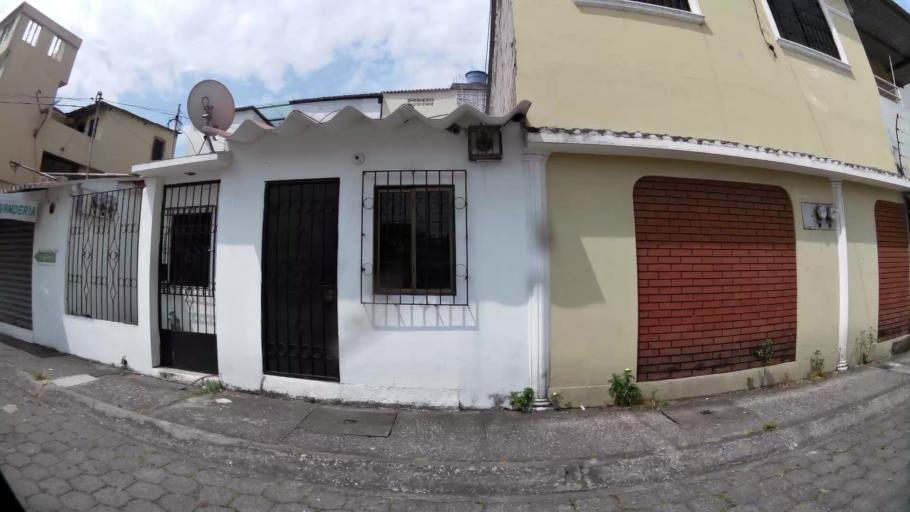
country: EC
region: Guayas
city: Eloy Alfaro
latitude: -2.1349
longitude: -79.9055
